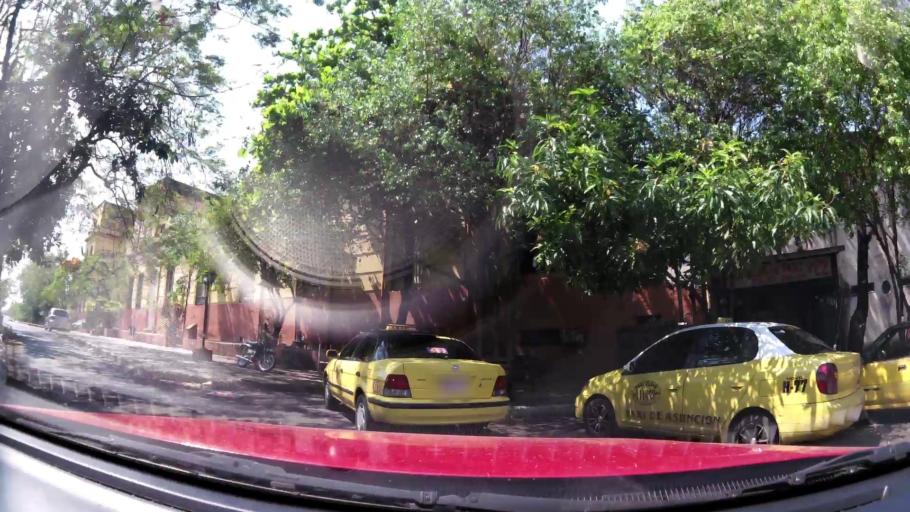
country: PY
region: Presidente Hayes
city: Nanawa
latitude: -25.2797
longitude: -57.6531
